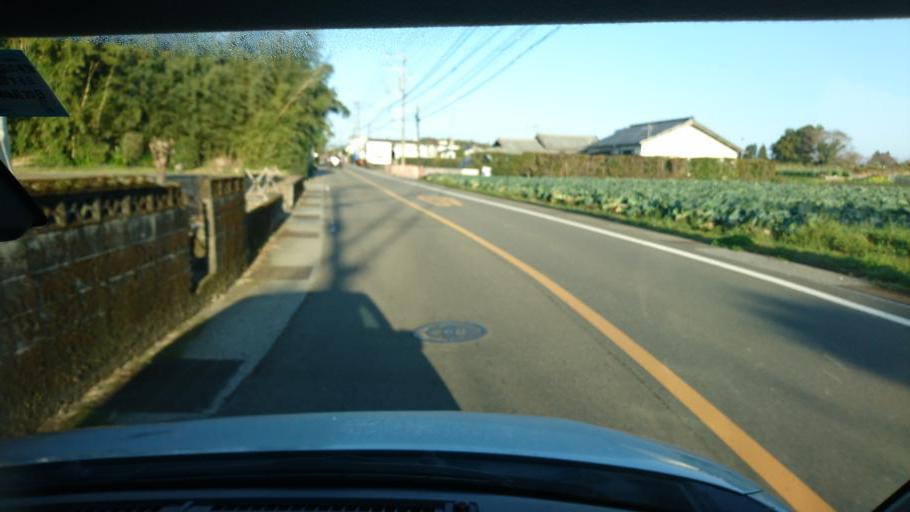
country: JP
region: Miyazaki
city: Miyazaki-shi
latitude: 31.8406
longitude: 131.4200
